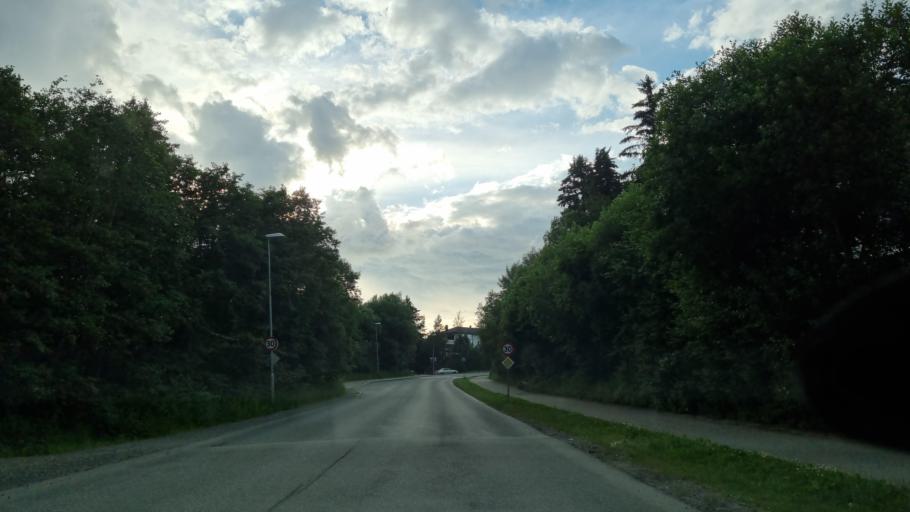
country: NO
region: Sor-Trondelag
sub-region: Trondheim
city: Trondheim
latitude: 63.3831
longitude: 10.3293
